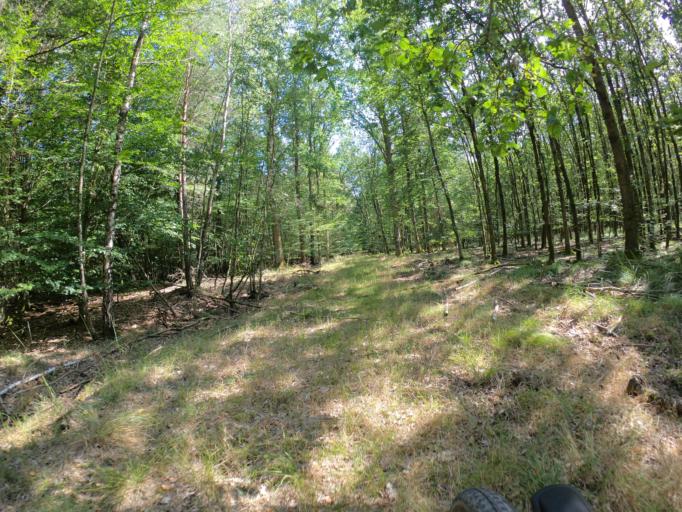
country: DE
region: Hesse
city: Langen
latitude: 50.0023
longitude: 8.6272
